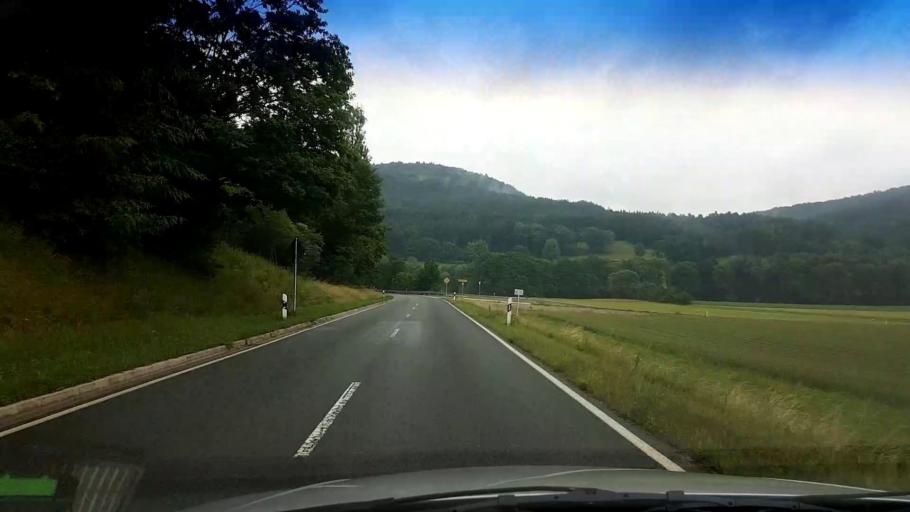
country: DE
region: Bavaria
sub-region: Upper Franconia
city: Weismain
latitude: 50.0707
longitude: 11.2173
